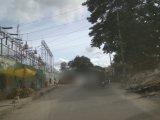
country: IN
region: Karnataka
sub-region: Bangalore Urban
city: Bangalore
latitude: 12.9923
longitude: 77.5511
